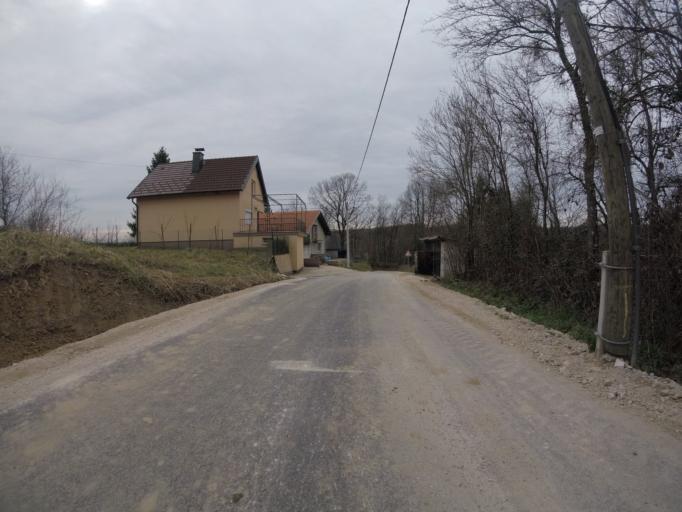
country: HR
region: Grad Zagreb
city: Strmec
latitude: 45.6081
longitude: 15.9101
